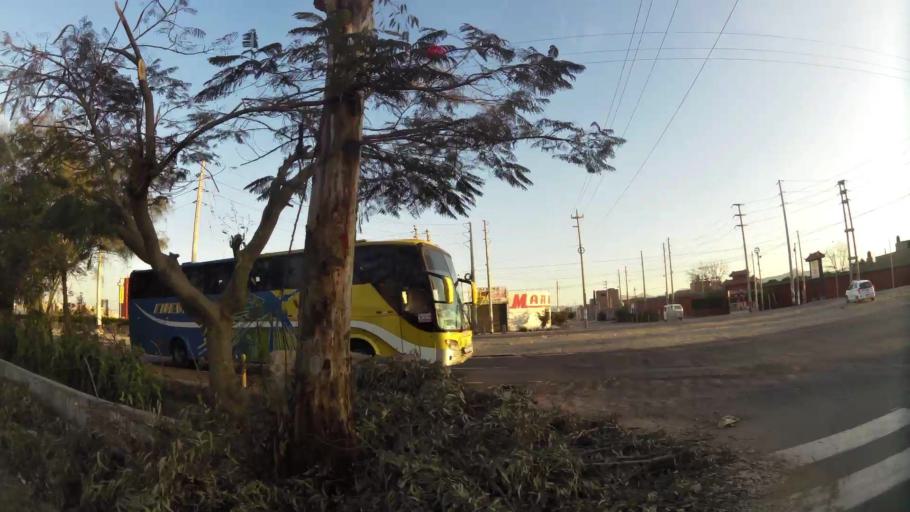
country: PE
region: Ica
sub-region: Provincia de Ica
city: Ica
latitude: -14.0868
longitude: -75.7276
